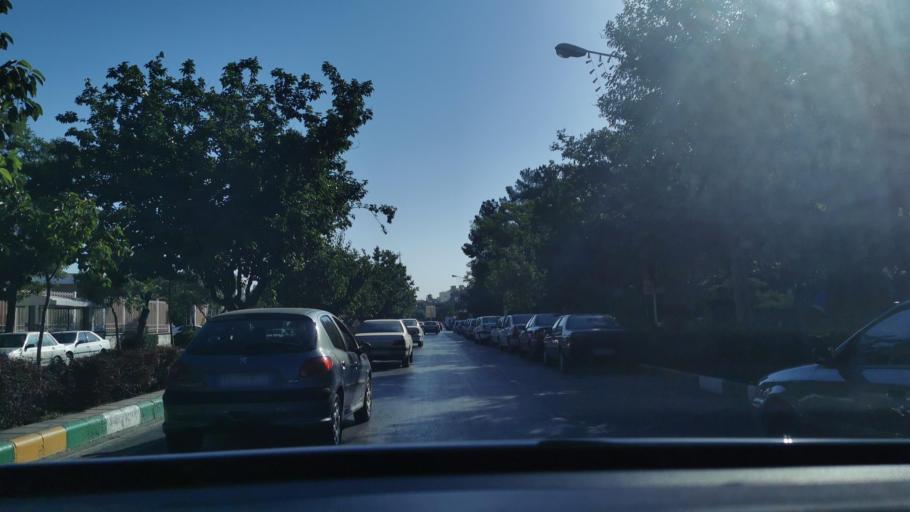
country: IR
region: Razavi Khorasan
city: Mashhad
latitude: 36.3182
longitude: 59.5232
